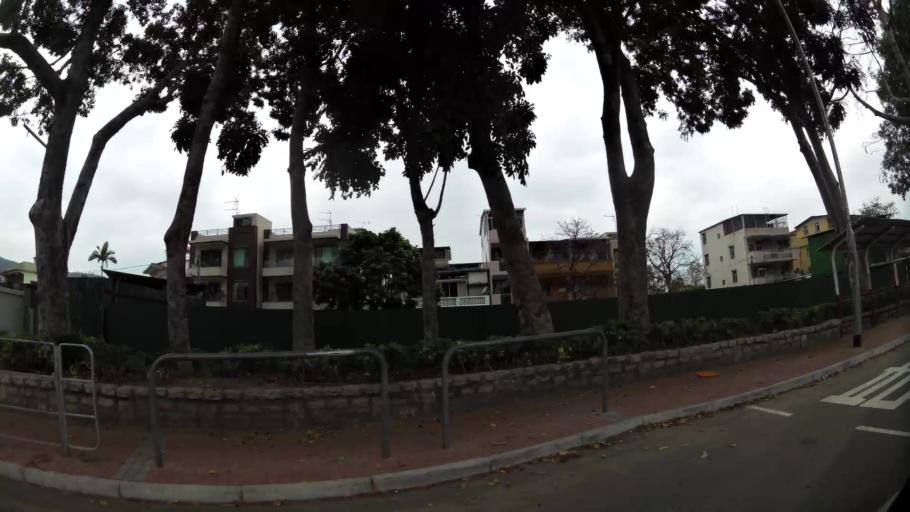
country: HK
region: Yuen Long
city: Yuen Long Kau Hui
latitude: 22.4452
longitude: 113.9923
